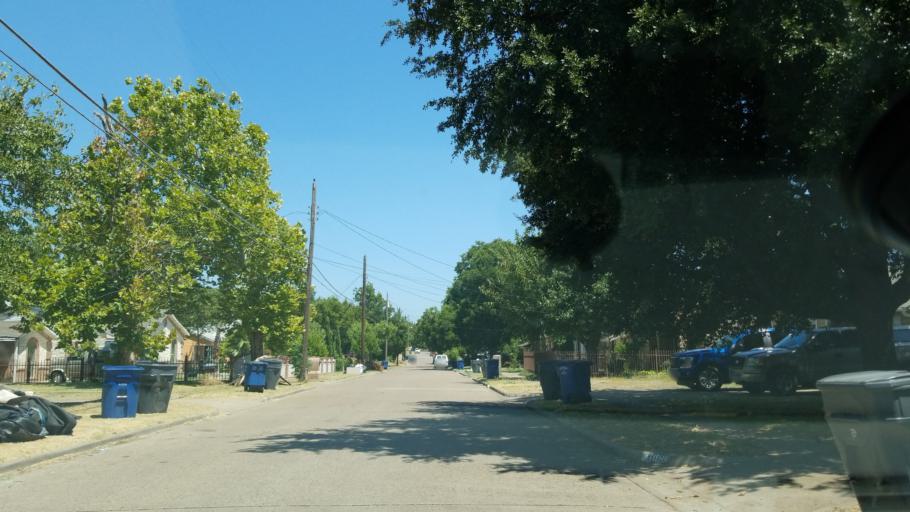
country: US
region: Texas
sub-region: Dallas County
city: Cockrell Hill
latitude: 32.7265
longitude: -96.8873
